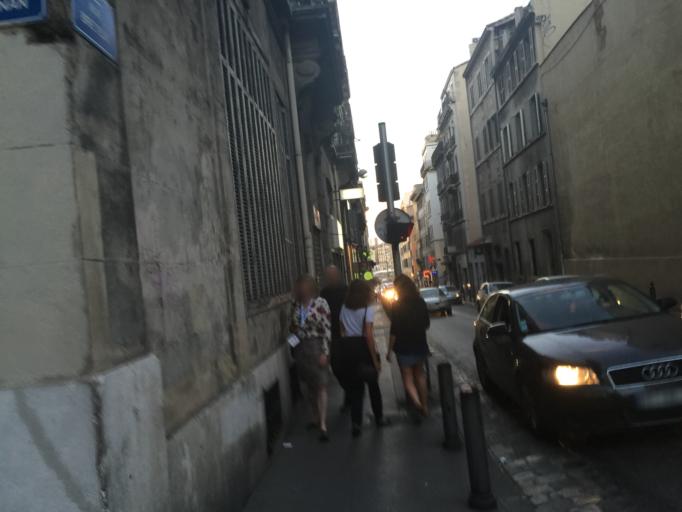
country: FR
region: Provence-Alpes-Cote d'Azur
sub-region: Departement des Bouches-du-Rhone
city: Marseille 06
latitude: 43.2918
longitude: 5.3752
